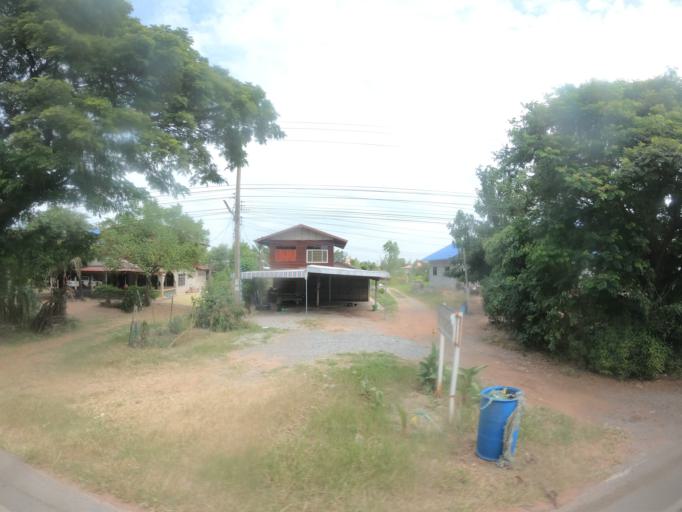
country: TH
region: Maha Sarakham
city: Chiang Yuen
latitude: 16.3526
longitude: 103.1179
